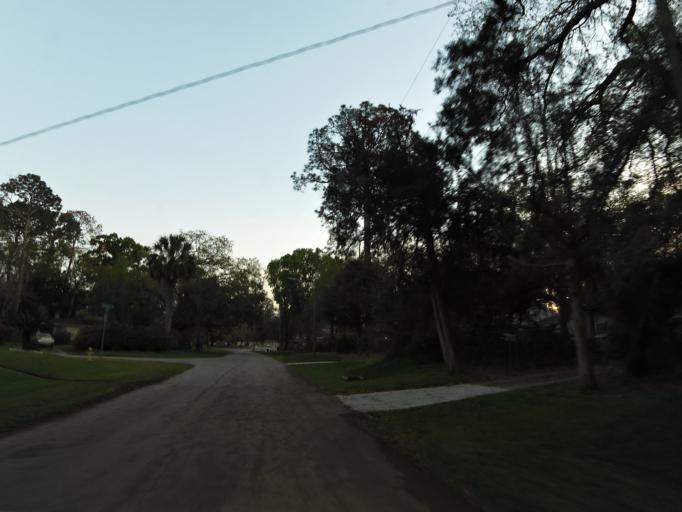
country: US
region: Florida
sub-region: Duval County
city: Jacksonville
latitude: 30.2894
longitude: -81.6232
